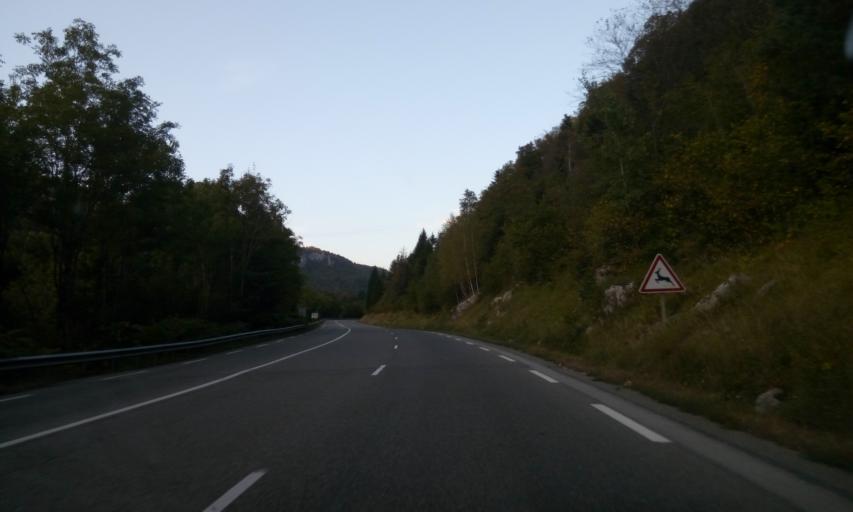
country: FR
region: Rhone-Alpes
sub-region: Departement de l'Ain
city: Nantua
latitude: 46.1459
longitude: 5.6420
